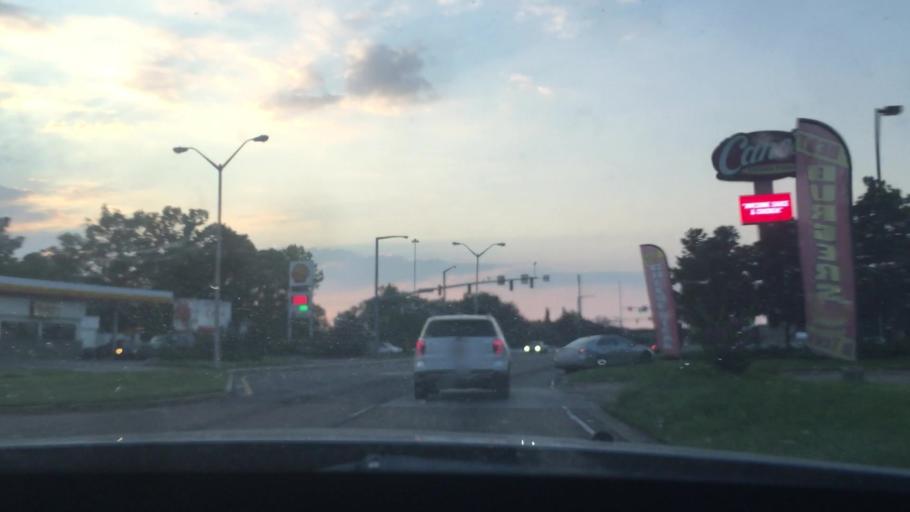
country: US
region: Louisiana
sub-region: East Baton Rouge Parish
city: Westminster
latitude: 30.4277
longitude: -91.0556
